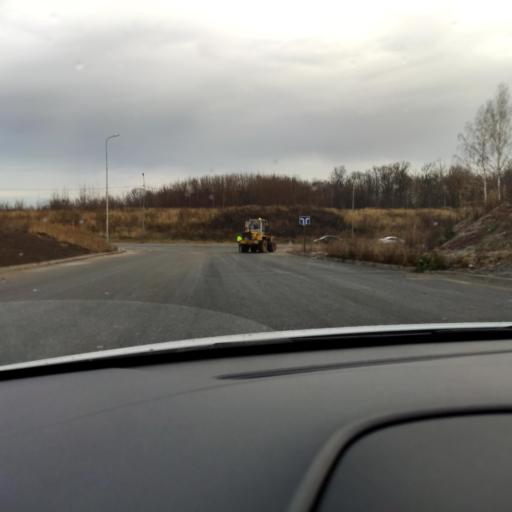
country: RU
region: Tatarstan
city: Osinovo
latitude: 55.8629
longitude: 48.8981
